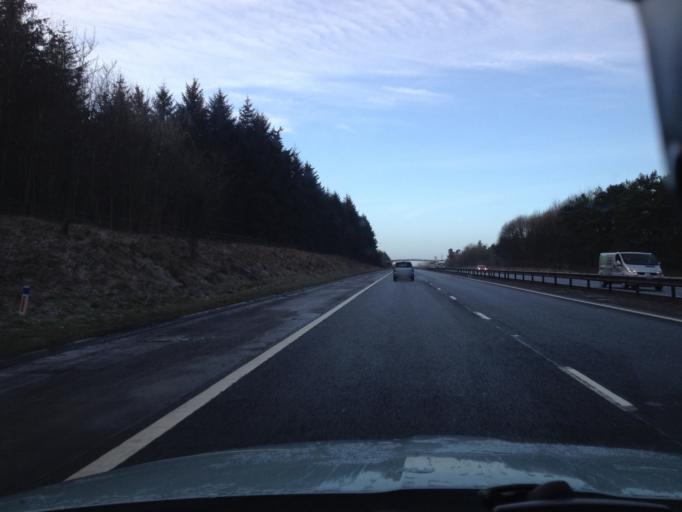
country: GB
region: Scotland
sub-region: West Lothian
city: Livingston
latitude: 55.9138
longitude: -3.5547
